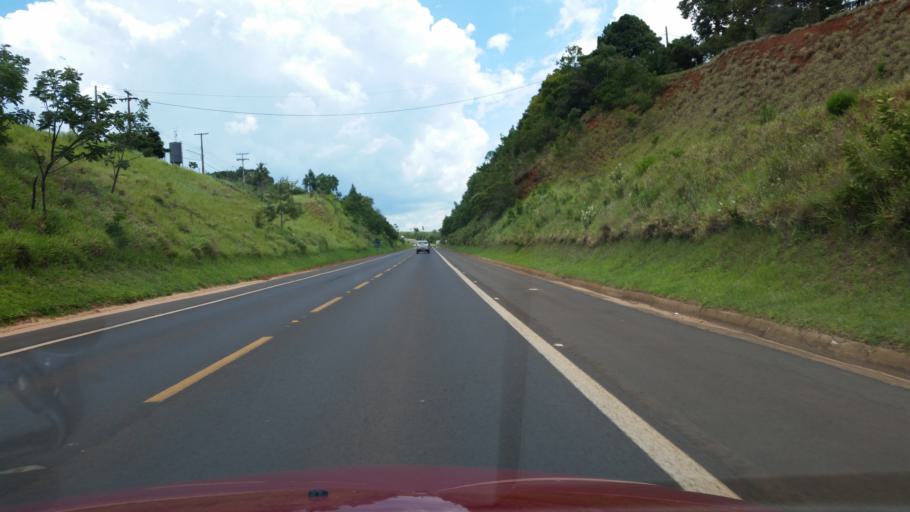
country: BR
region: Sao Paulo
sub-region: Itai
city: Itai
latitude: -23.2746
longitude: -49.0186
